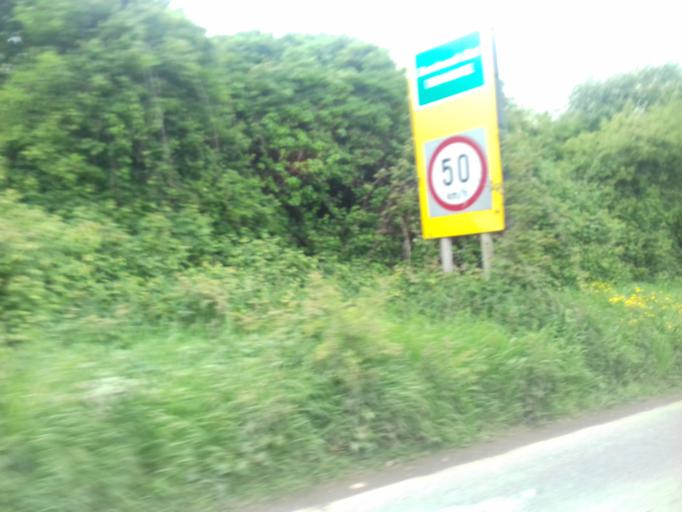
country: IE
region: Leinster
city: Donabate
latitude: 53.4839
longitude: -6.1431
